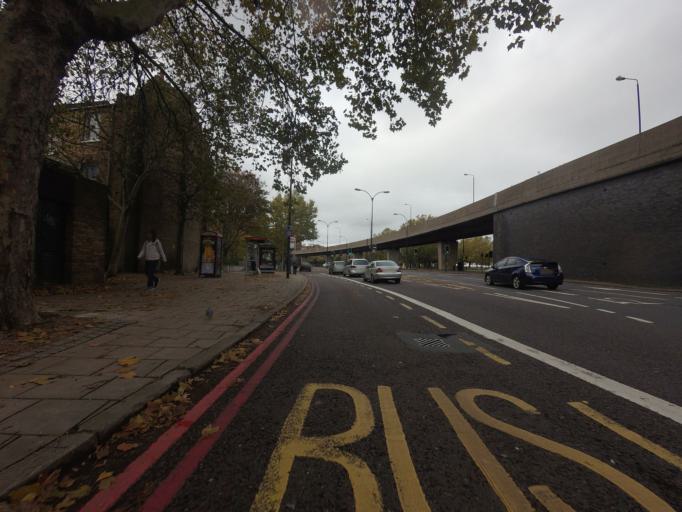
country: GB
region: England
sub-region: Greater London
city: City of London
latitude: 51.4935
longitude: -0.0849
